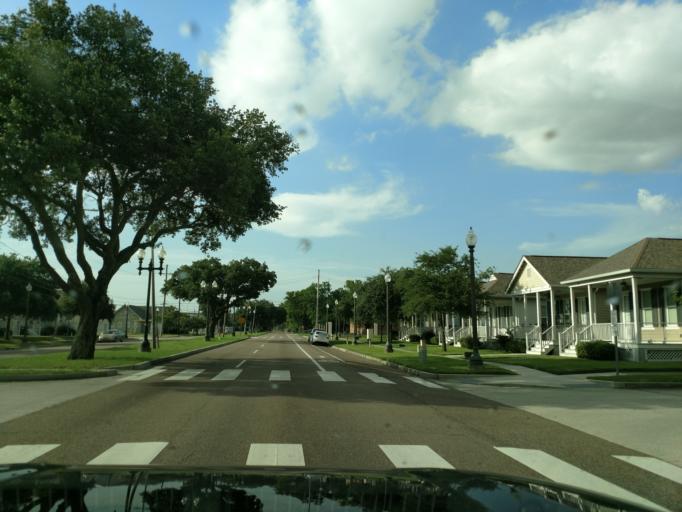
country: US
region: Louisiana
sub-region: Jefferson Parish
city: Gretna
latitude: 29.9328
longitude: -90.0416
